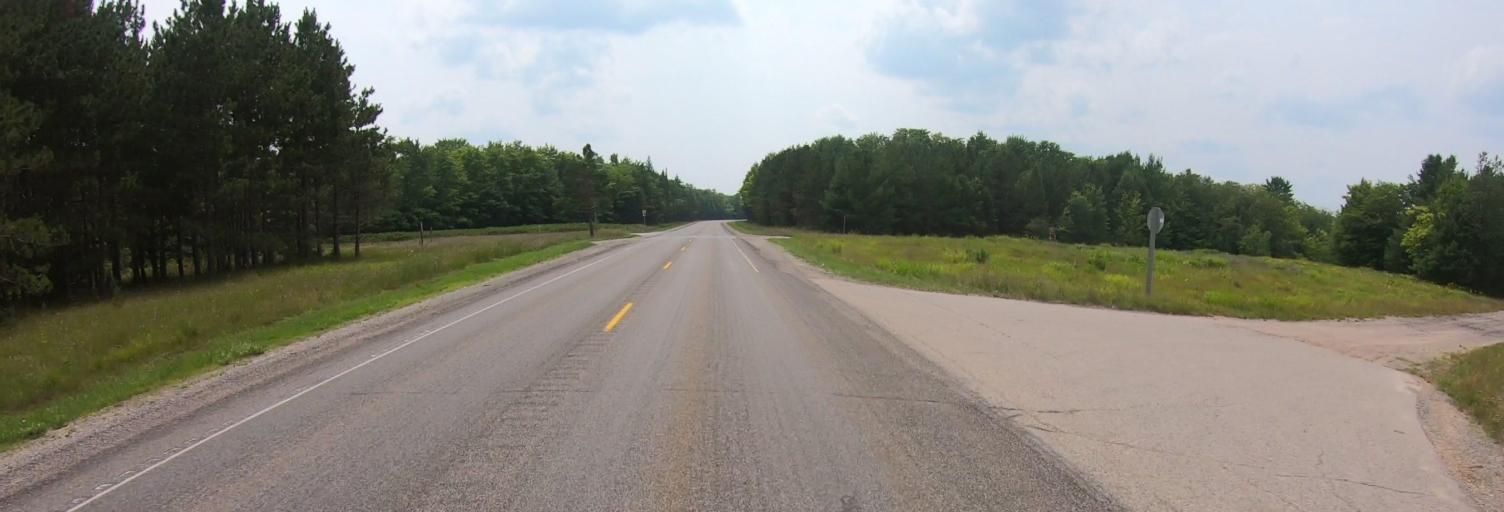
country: US
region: Michigan
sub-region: Alger County
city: Munising
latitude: 46.3411
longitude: -86.7322
